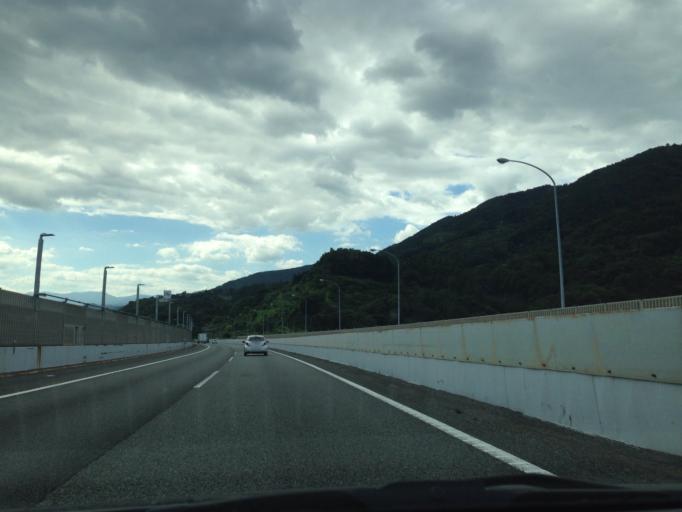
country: JP
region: Kanagawa
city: Hadano
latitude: 35.3473
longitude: 139.1511
